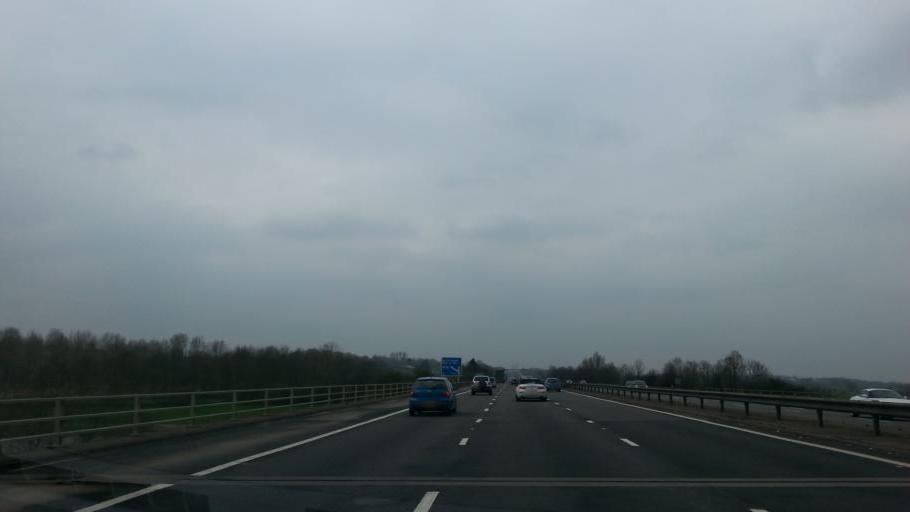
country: GB
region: England
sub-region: Worcestershire
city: Bredon
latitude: 52.0335
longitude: -2.1272
